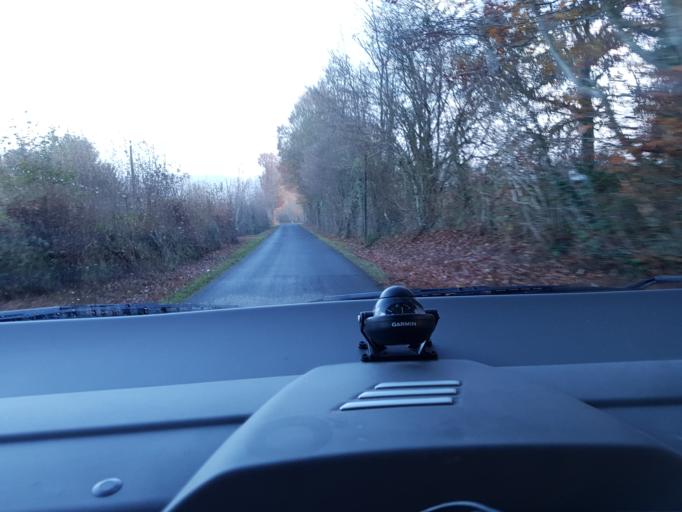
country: FR
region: Lower Normandy
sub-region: Departement de l'Orne
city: La Ferriere-aux-Etangs
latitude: 48.6363
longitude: -0.4772
